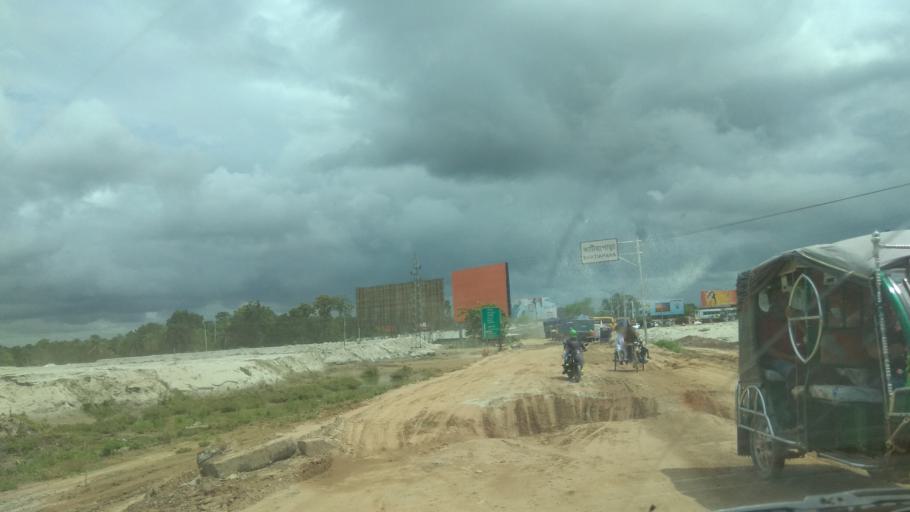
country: BD
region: Khulna
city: Kalia
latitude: 23.2118
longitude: 89.7093
